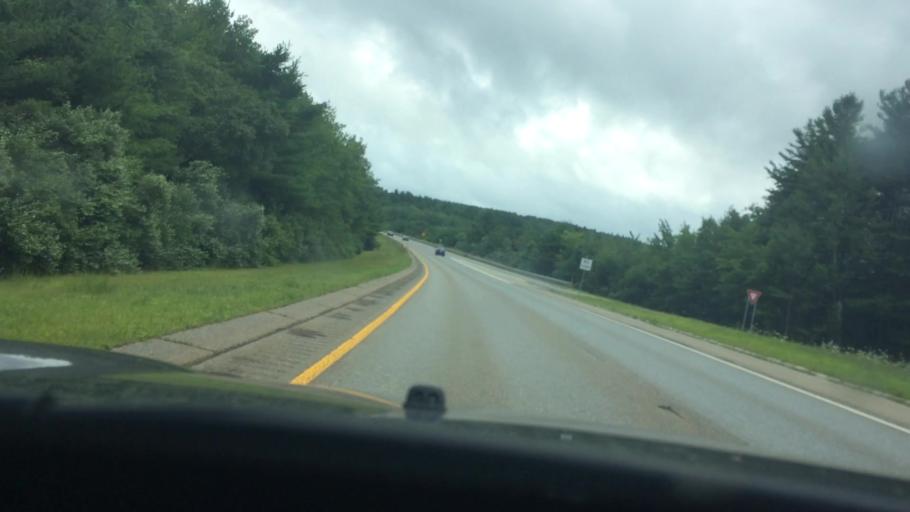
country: US
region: Massachusetts
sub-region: Worcester County
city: Templeton
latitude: 42.5563
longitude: -72.0446
